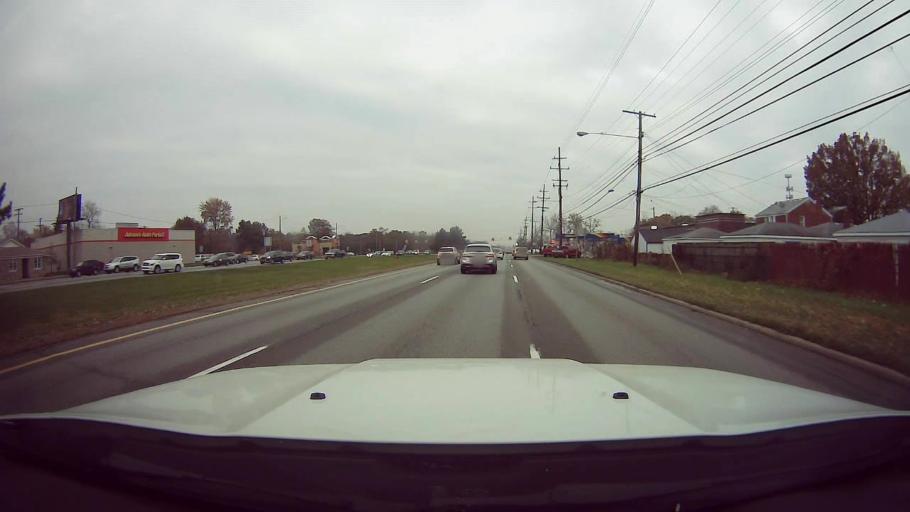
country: US
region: Michigan
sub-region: Wayne County
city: Dearborn Heights
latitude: 42.3513
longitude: -83.2743
